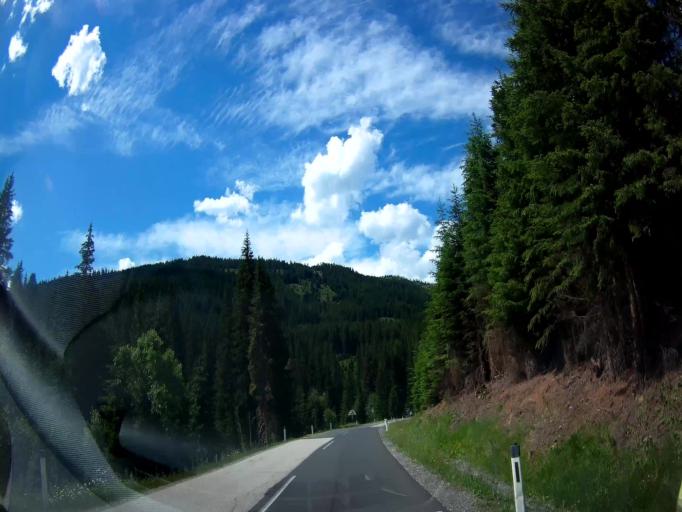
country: AT
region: Styria
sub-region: Politischer Bezirk Murau
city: Stadl an der Mur
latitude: 46.9771
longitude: 14.0070
